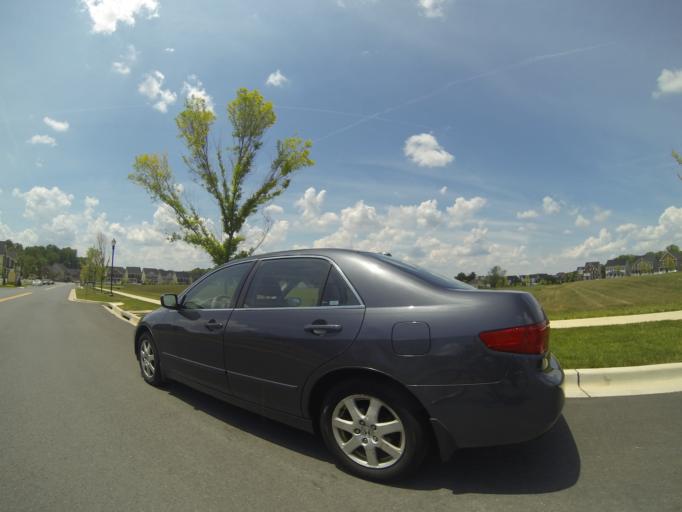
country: US
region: Maryland
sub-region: Montgomery County
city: Clarksburg
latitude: 39.2243
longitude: -77.2429
